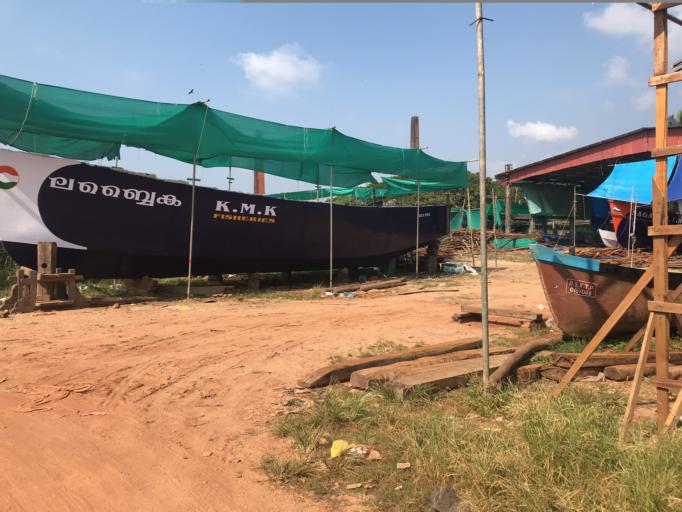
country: IN
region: Karnataka
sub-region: Dakshina Kannada
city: Ullal
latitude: 12.8507
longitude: 74.8350
